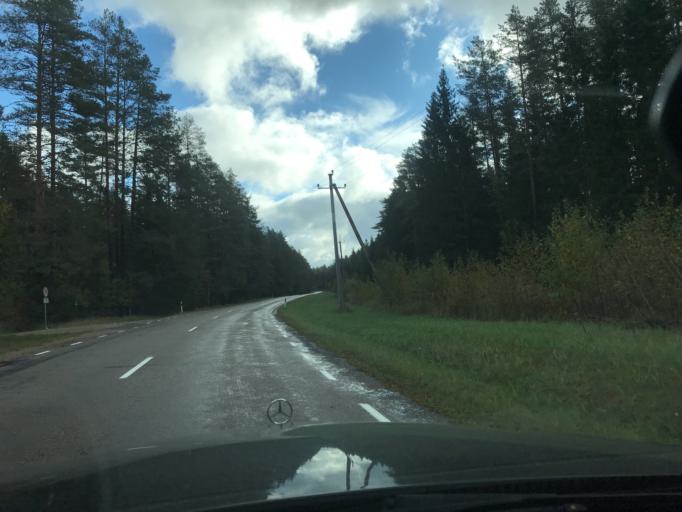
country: EE
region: Valgamaa
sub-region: Torva linn
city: Torva
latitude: 58.0118
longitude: 26.1189
